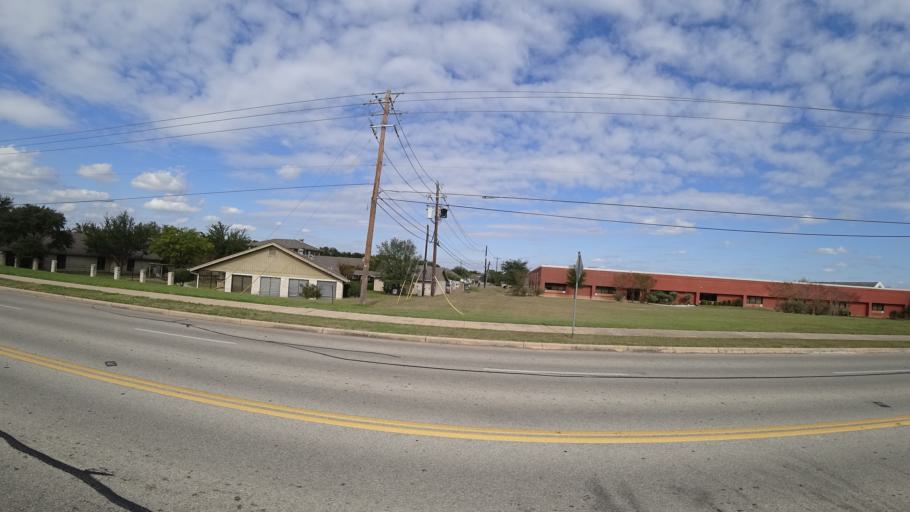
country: US
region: Texas
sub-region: Travis County
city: Windemere
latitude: 30.4423
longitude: -97.6423
